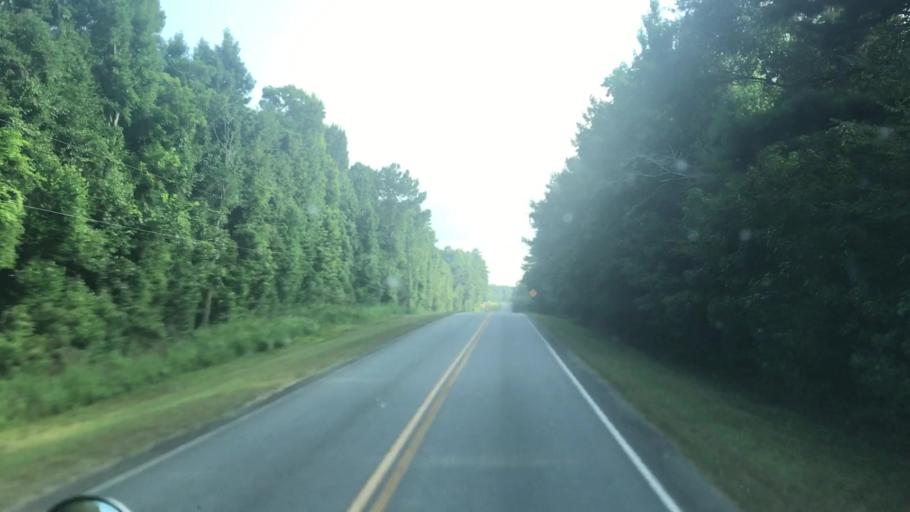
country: US
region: Florida
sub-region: Gadsden County
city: Havana
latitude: 30.7211
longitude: -84.4877
